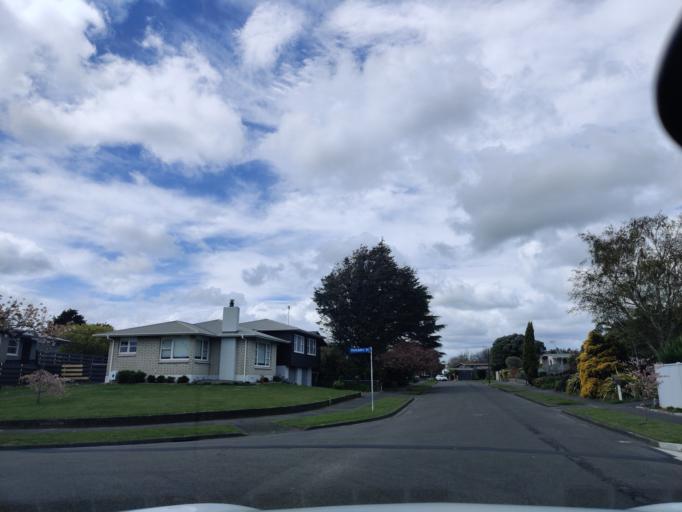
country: NZ
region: Manawatu-Wanganui
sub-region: Palmerston North City
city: Palmerston North
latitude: -40.3808
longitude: 175.5934
